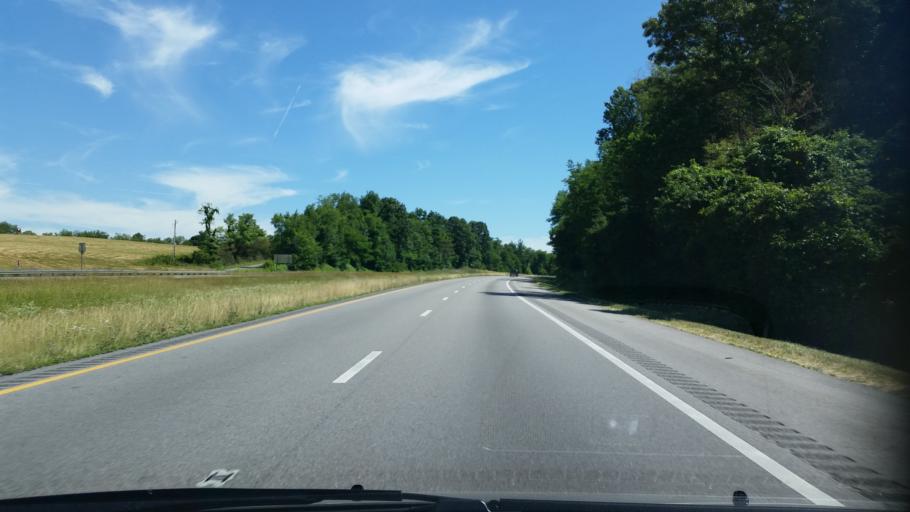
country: US
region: Virginia
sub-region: Washington County
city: Abingdon
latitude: 36.7316
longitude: -81.9064
